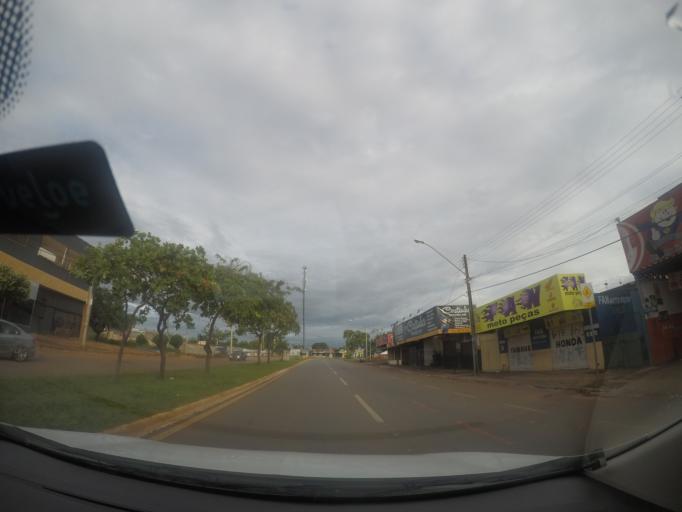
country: BR
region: Goias
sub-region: Goiania
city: Goiania
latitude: -16.6249
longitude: -49.3353
